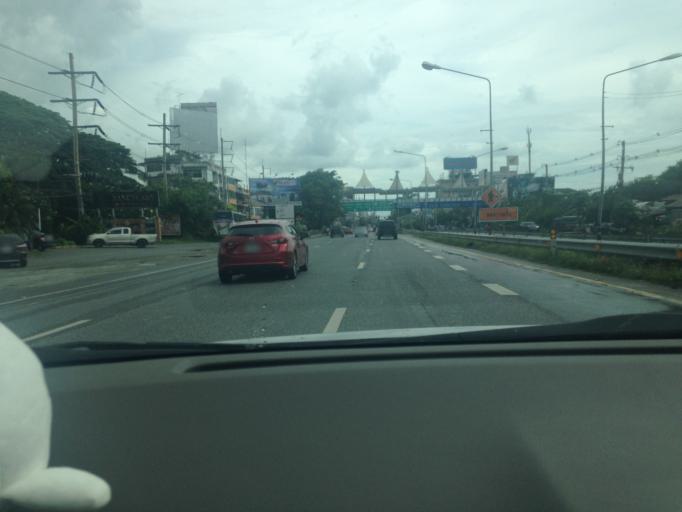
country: TH
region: Chon Buri
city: Chon Buri
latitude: 13.2891
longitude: 100.9411
